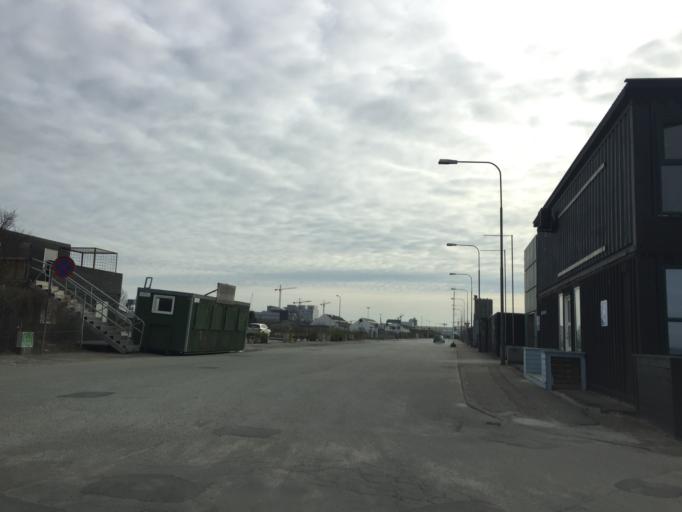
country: DK
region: Capital Region
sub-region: Gentofte Kommune
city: Charlottenlund
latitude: 55.7188
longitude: 12.5986
